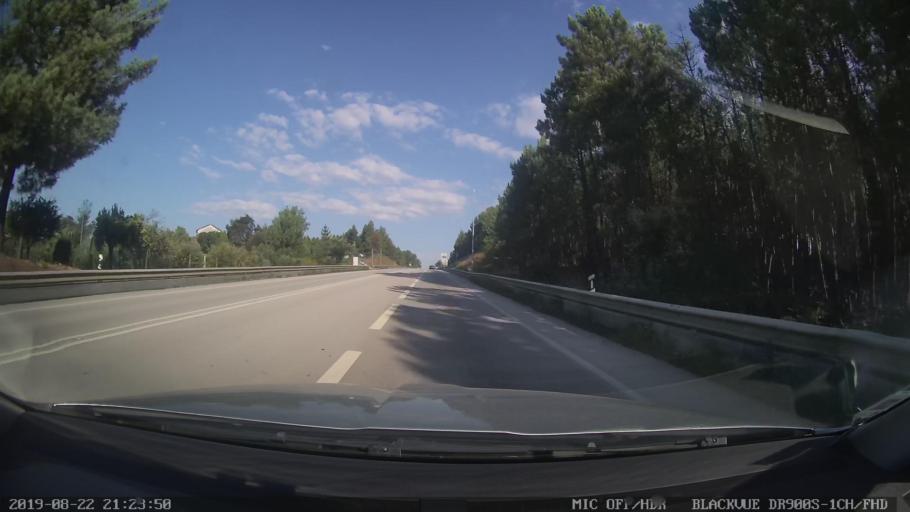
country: PT
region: Castelo Branco
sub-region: Serta
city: Serta
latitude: 39.8356
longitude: -8.1131
